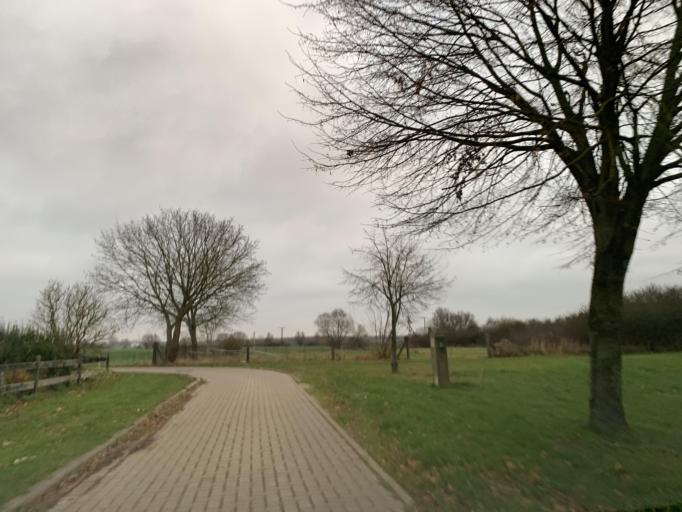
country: DE
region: Mecklenburg-Vorpommern
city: Blankensee
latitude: 53.3939
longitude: 13.3109
